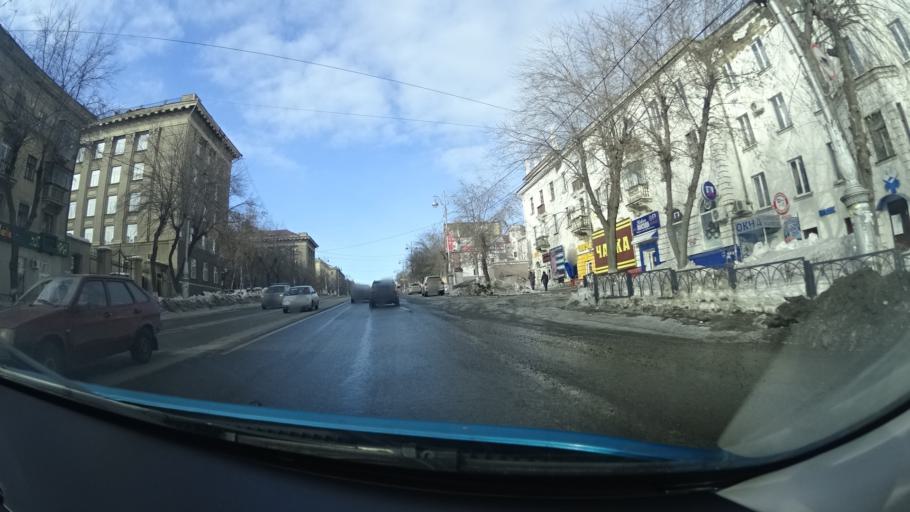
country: RU
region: Chelyabinsk
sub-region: Gorod Magnitogorsk
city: Magnitogorsk
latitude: 53.4262
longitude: 58.9837
